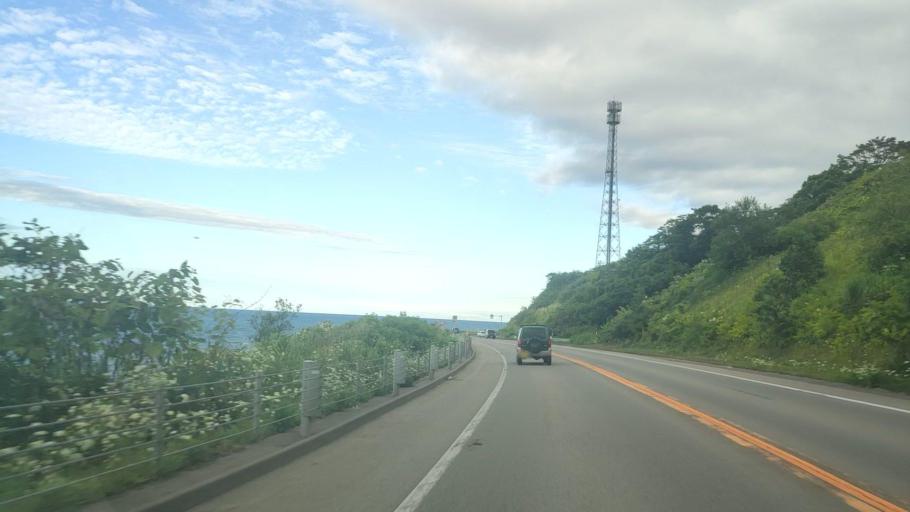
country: JP
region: Hokkaido
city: Nanae
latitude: 42.1995
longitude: 140.4130
